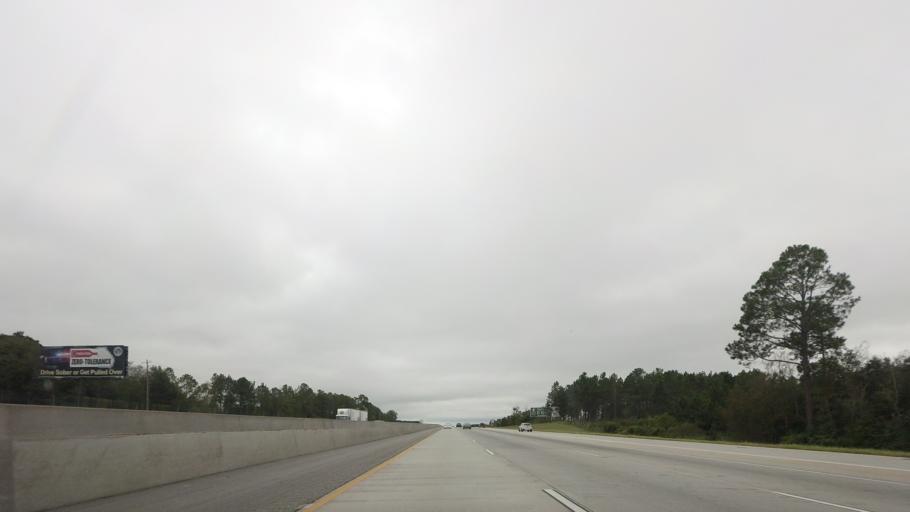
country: US
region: Georgia
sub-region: Tift County
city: Unionville
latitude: 31.3502
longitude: -83.4880
